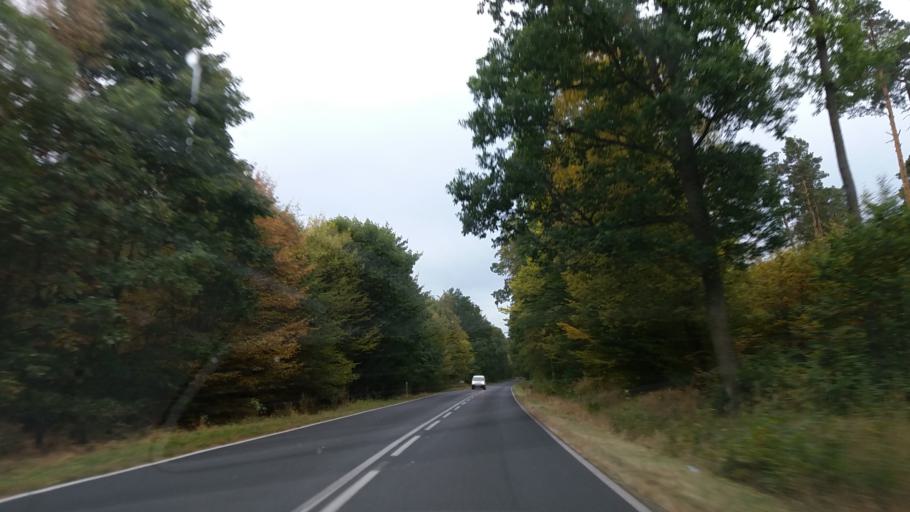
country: PL
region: West Pomeranian Voivodeship
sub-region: Powiat mysliborski
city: Barlinek
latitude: 52.9000
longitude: 15.1928
